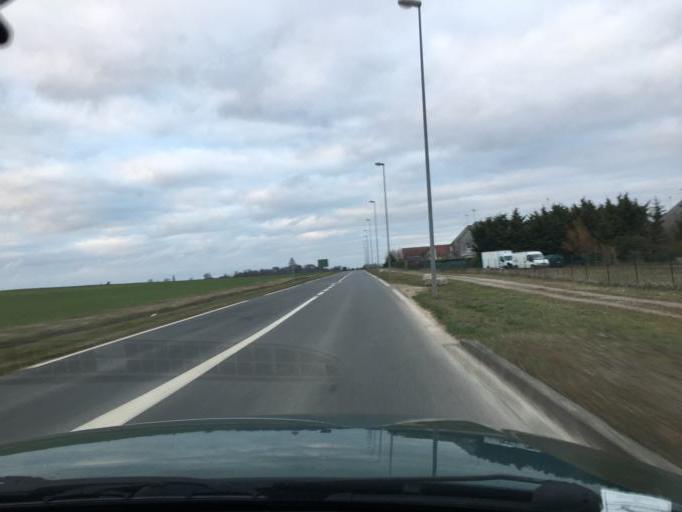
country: FR
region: Centre
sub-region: Departement du Loiret
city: Beaugency
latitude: 47.7857
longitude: 1.6144
